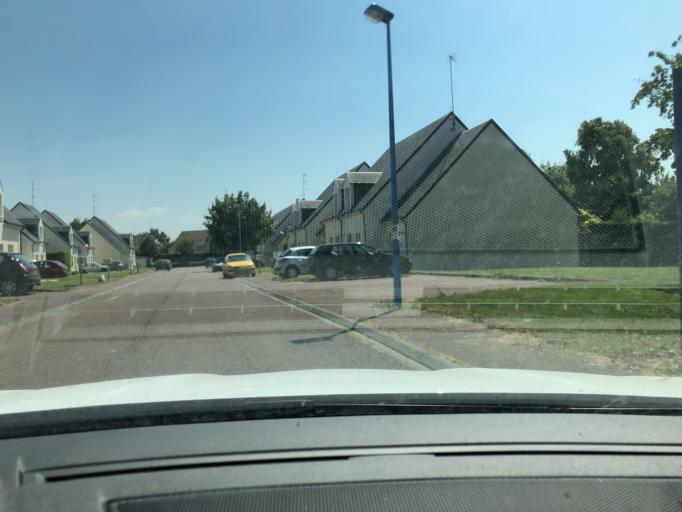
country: FR
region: Lower Normandy
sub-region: Departement du Calvados
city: Lion-sur-Mer
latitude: 49.2994
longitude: -0.3256
